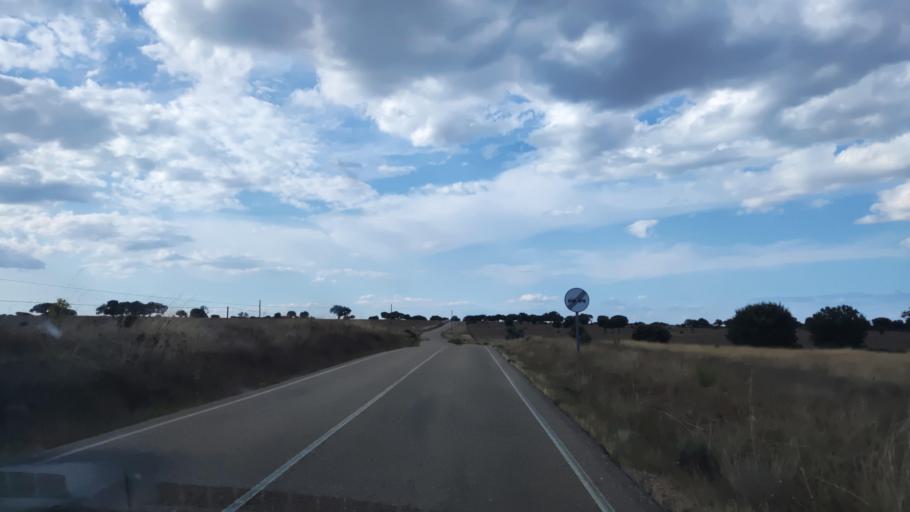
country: ES
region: Castille and Leon
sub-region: Provincia de Salamanca
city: Martiago
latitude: 40.4798
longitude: -6.4916
